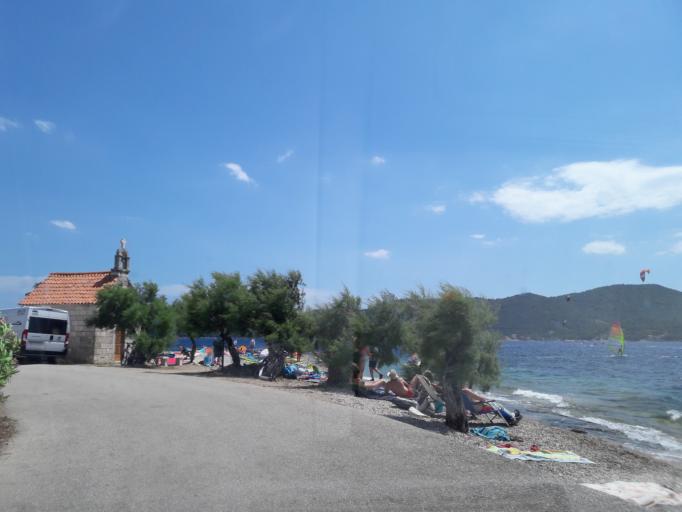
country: HR
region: Dubrovacko-Neretvanska
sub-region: Grad Korcula
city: Zrnovo
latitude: 42.9793
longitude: 17.1031
